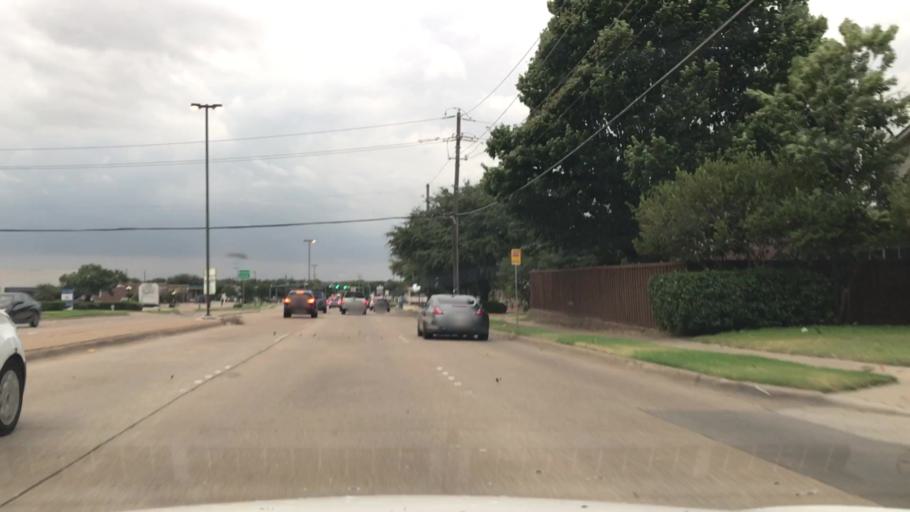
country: US
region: Texas
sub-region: Dallas County
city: Carrollton
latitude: 33.0147
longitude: -96.8871
